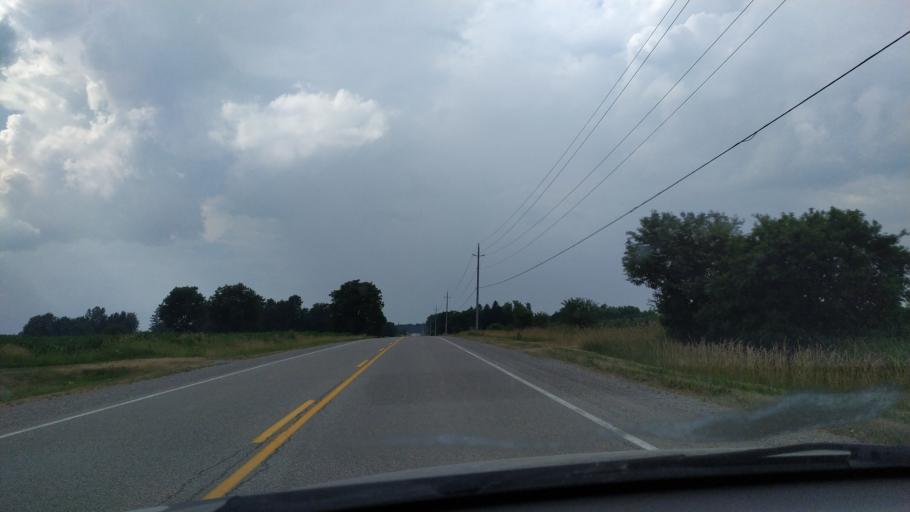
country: CA
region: Ontario
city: London
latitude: 43.2129
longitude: -81.1591
